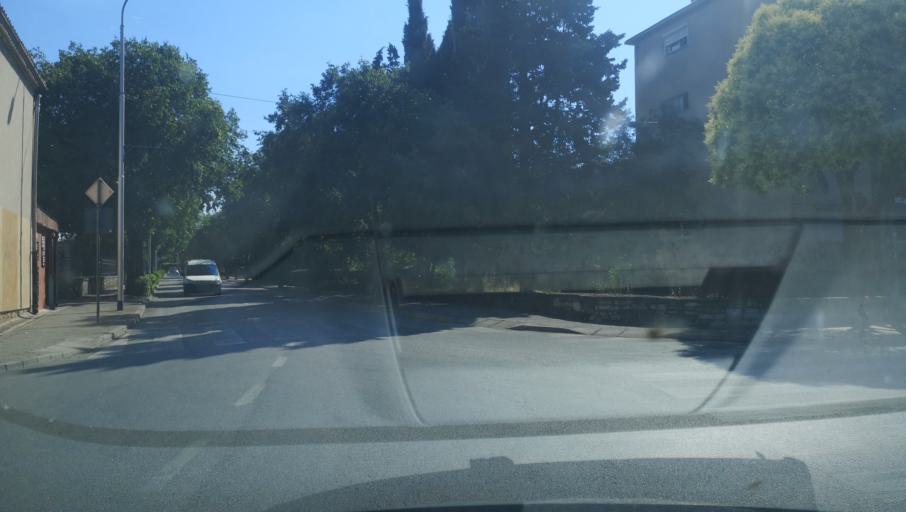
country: HR
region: Istarska
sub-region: Grad Rovinj
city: Rovinj
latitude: 45.0787
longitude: 13.6428
